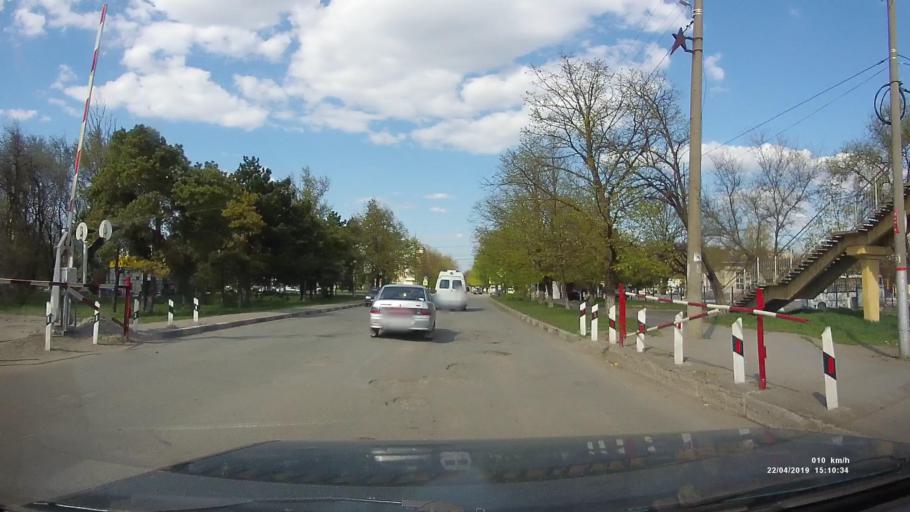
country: RU
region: Rostov
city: Azov
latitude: 47.1007
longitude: 39.4119
